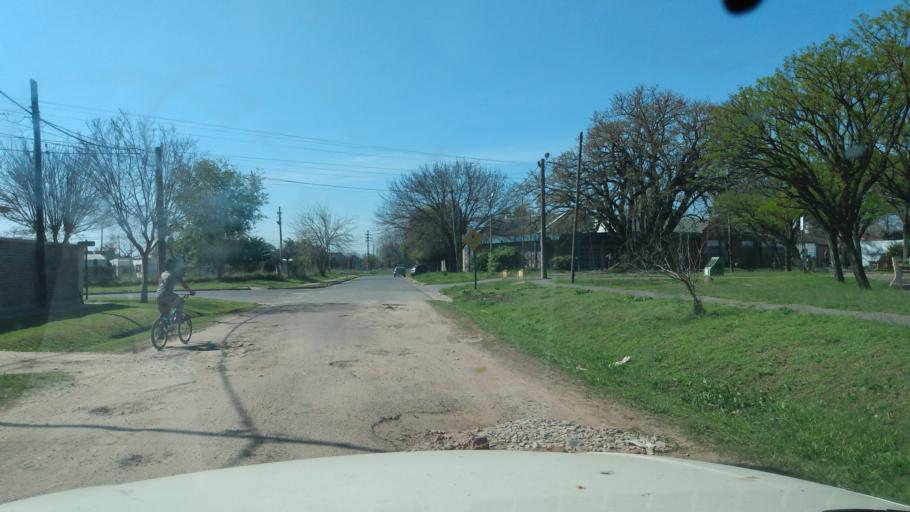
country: AR
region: Buenos Aires
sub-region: Partido de Lujan
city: Lujan
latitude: -34.5778
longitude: -59.1015
